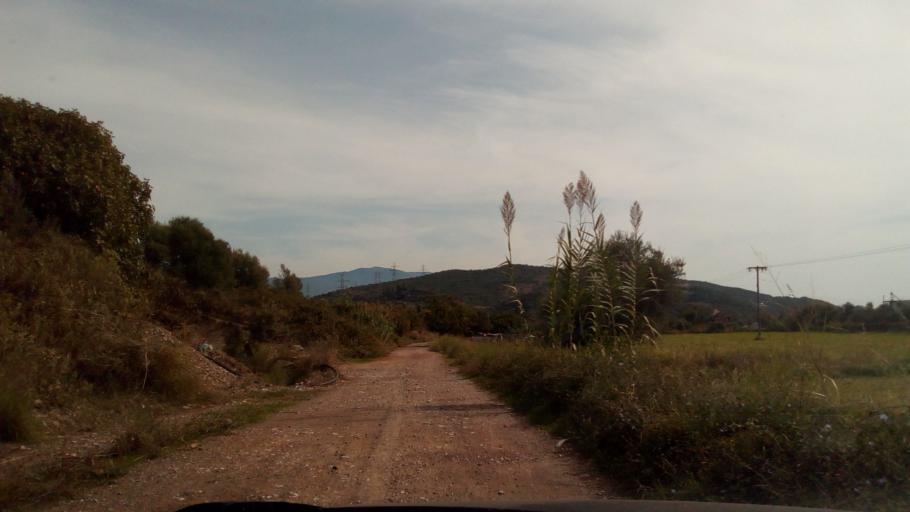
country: GR
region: West Greece
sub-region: Nomos Aitolias kai Akarnanias
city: Nafpaktos
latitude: 38.4100
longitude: 21.8893
